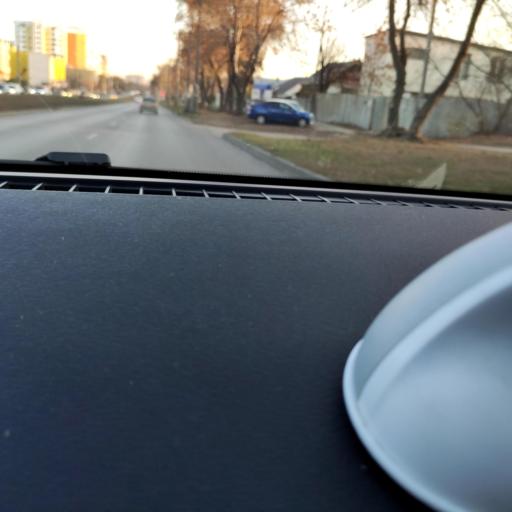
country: RU
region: Samara
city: Samara
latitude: 53.2310
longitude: 50.2255
